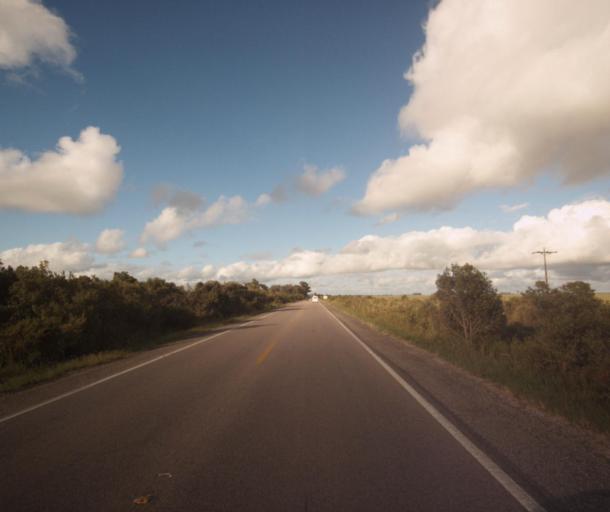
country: BR
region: Rio Grande do Sul
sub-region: Rio Grande
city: Rio Grande
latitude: -32.1878
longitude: -52.4306
